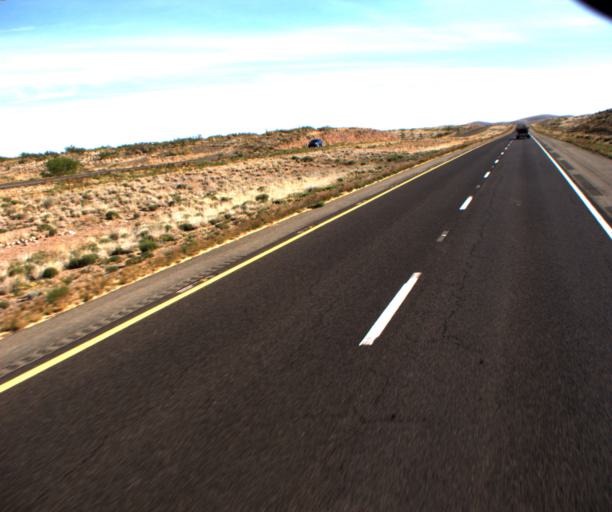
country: US
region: Arizona
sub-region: Cochise County
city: Willcox
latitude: 32.3680
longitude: -109.6770
